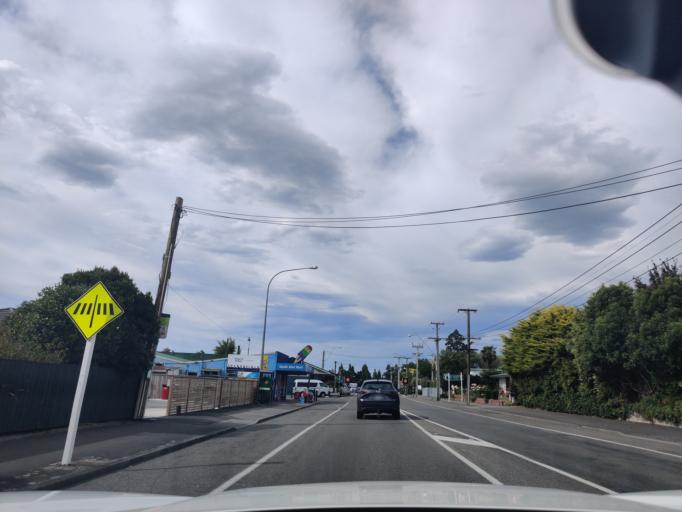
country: NZ
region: Wellington
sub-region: Masterton District
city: Masterton
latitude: -40.9428
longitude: 175.6697
